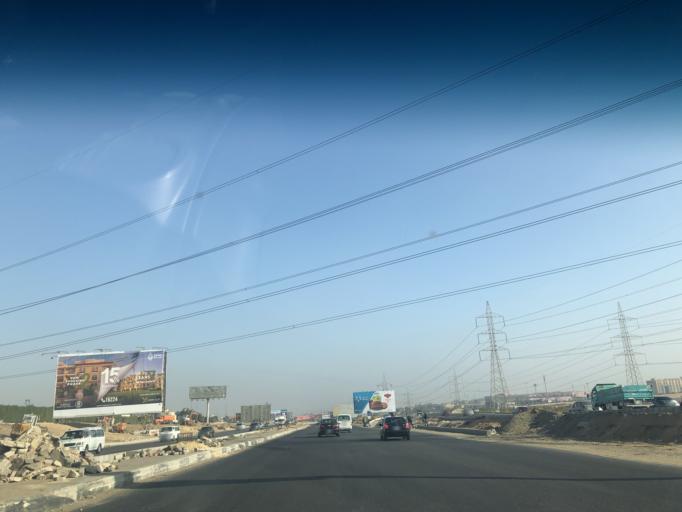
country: EG
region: Al Jizah
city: Madinat Sittah Uktubar
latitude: 29.9732
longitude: 31.0043
